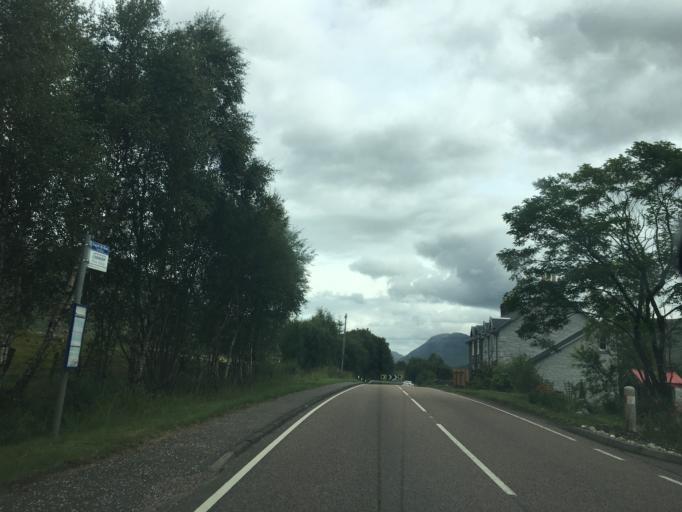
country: GB
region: Scotland
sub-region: Argyll and Bute
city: Garelochhead
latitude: 56.4093
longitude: -5.0308
